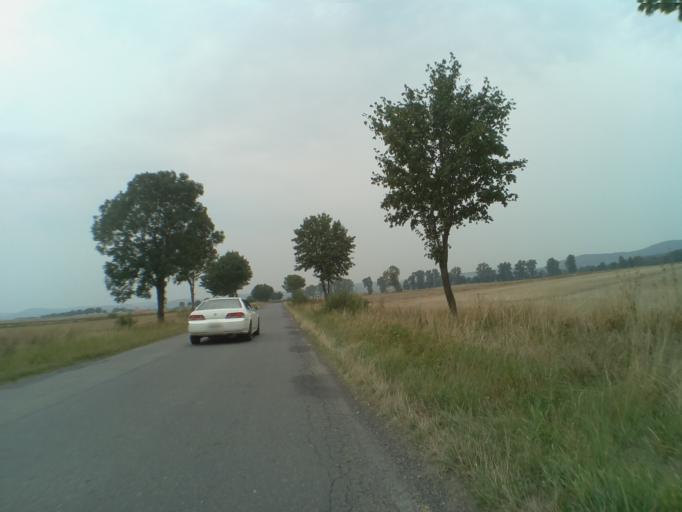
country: PL
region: Lower Silesian Voivodeship
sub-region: Powiat swidnicki
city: Swiebodzice
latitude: 50.8923
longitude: 16.3221
